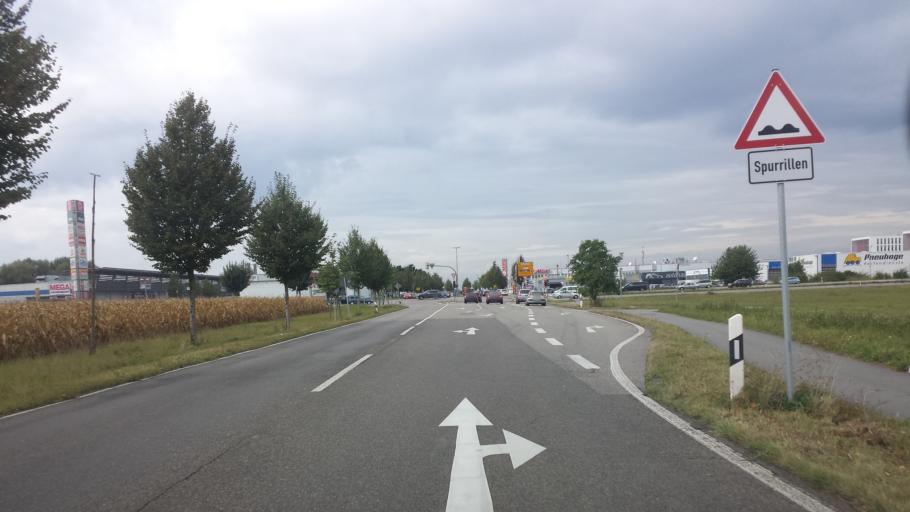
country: DE
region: Baden-Wuerttemberg
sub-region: Karlsruhe Region
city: Forst
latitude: 49.1355
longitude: 8.5740
